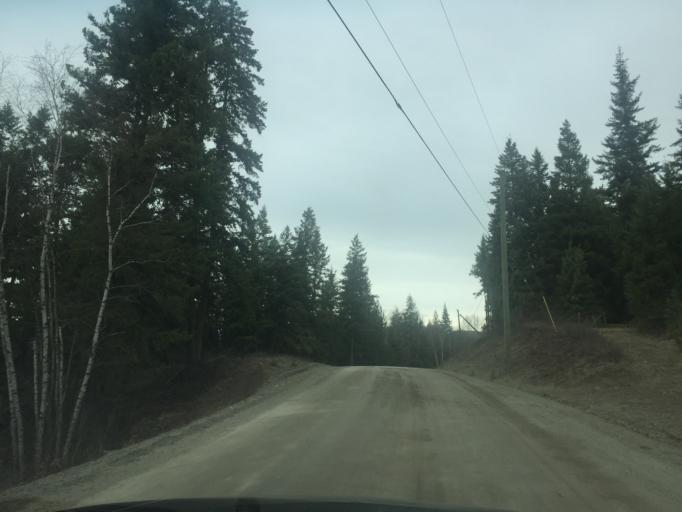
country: CA
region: British Columbia
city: Kamloops
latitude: 51.3281
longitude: -120.1492
